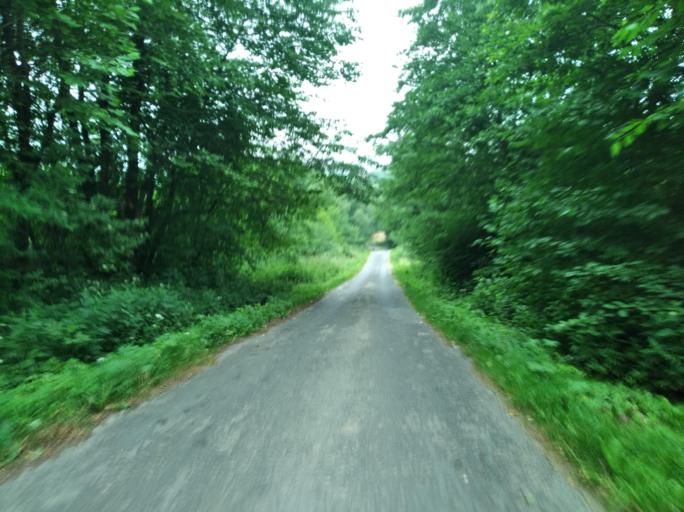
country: PL
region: Subcarpathian Voivodeship
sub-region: Powiat brzozowski
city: Jasienica Rosielna
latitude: 49.7562
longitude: 21.9251
